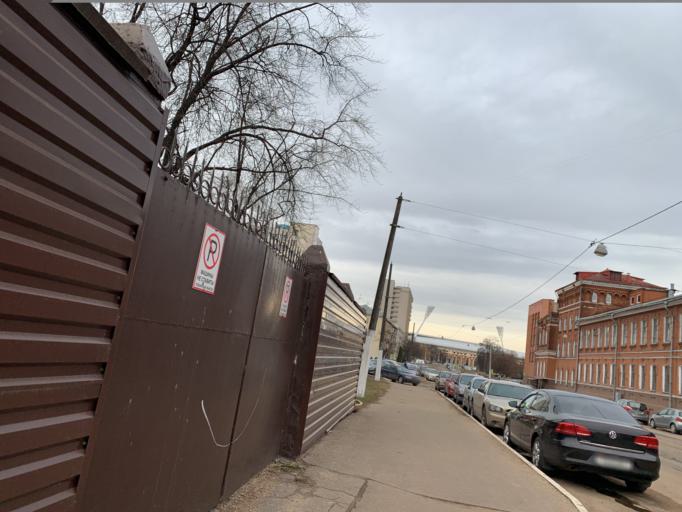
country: BY
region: Minsk
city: Minsk
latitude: 53.8918
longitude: 27.5696
